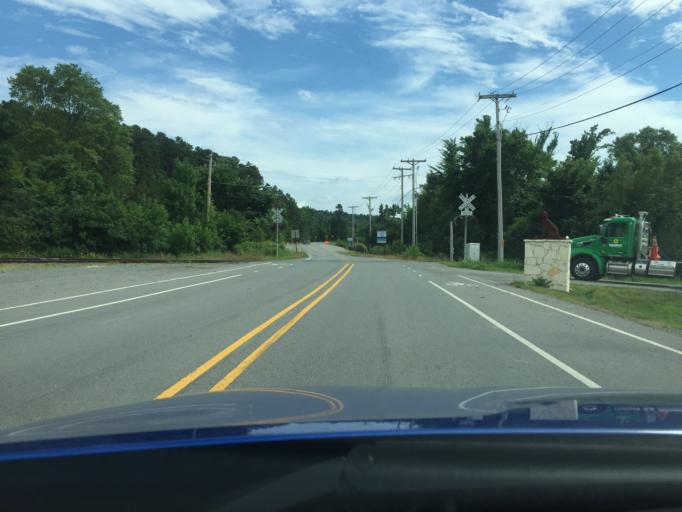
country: US
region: Arkansas
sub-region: Pulaski County
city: Maumelle
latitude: 34.8138
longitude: -92.4431
